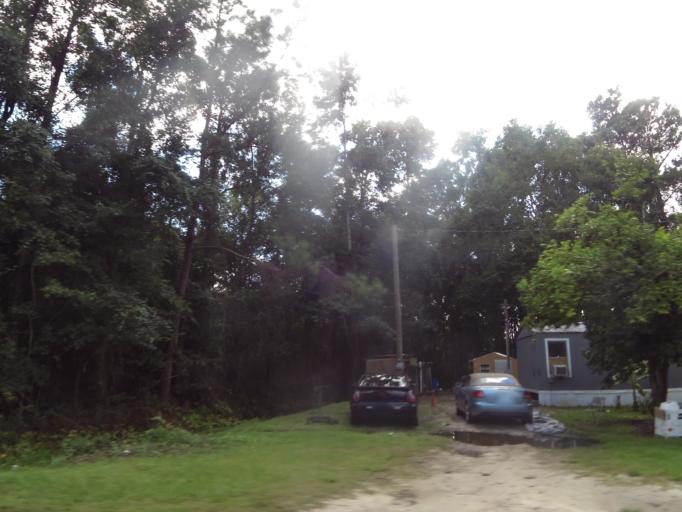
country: US
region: Georgia
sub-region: Camden County
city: Kingsland
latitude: 30.8031
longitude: -81.6936
